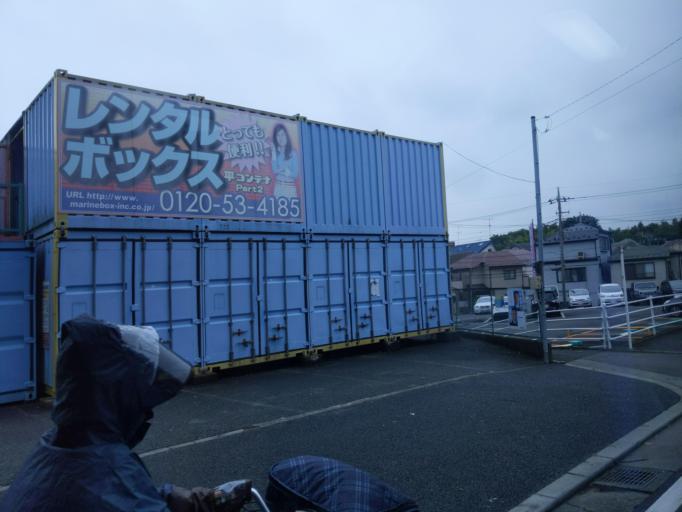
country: JP
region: Tokyo
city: Chofugaoka
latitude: 35.5983
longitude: 139.5718
